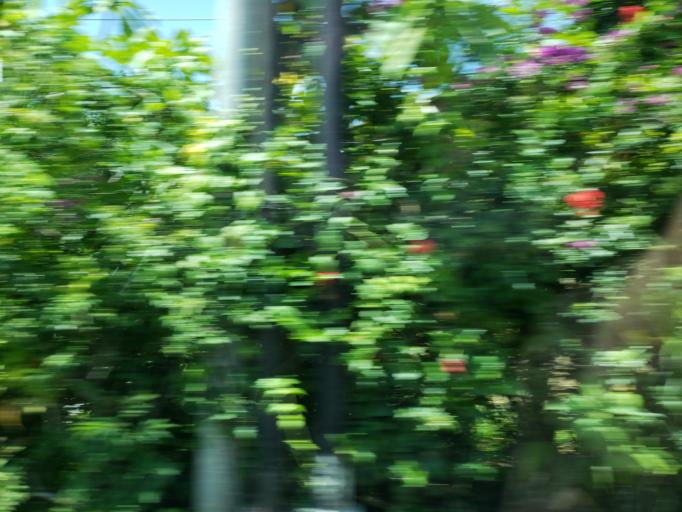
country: ID
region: Bali
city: Kangin
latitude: -8.8362
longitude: 115.1364
